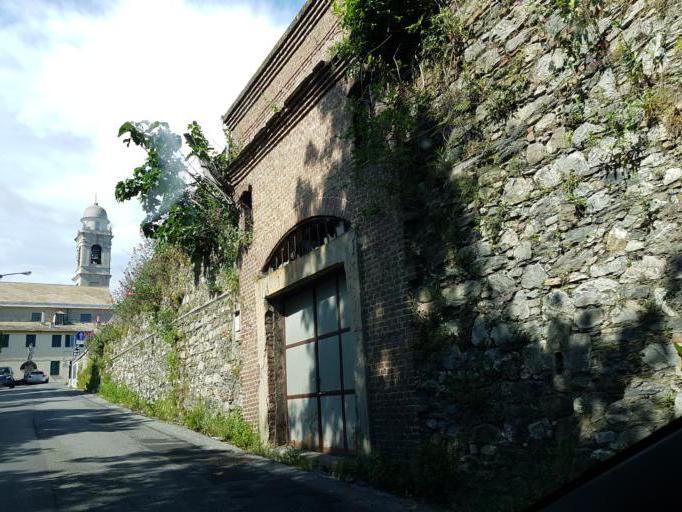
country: IT
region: Liguria
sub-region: Provincia di Genova
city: Manesseno
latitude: 44.4605
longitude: 8.8892
